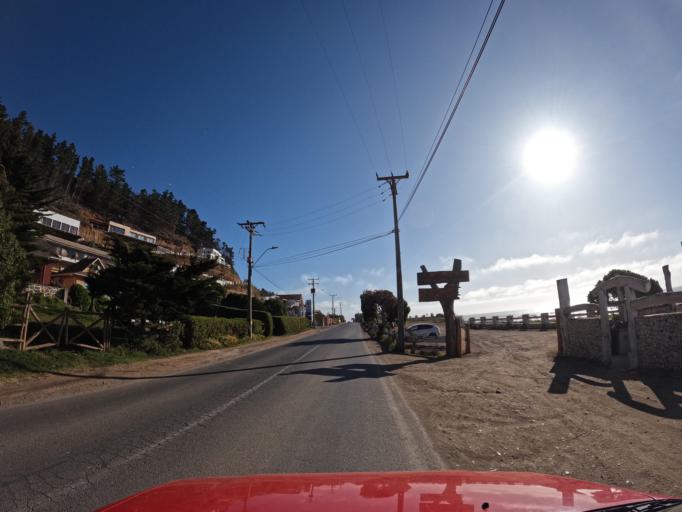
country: CL
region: Maule
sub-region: Provincia de Talca
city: Constitucion
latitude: -34.8870
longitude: -72.1699
